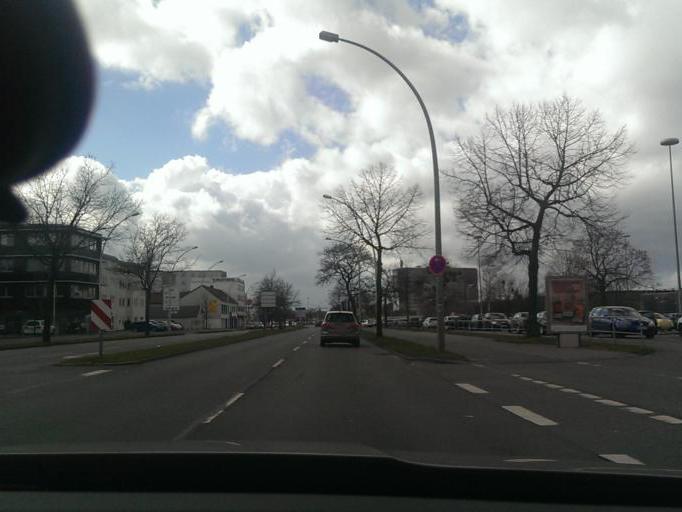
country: DE
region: Lower Saxony
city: Wolfsburg
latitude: 52.4281
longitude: 10.7799
